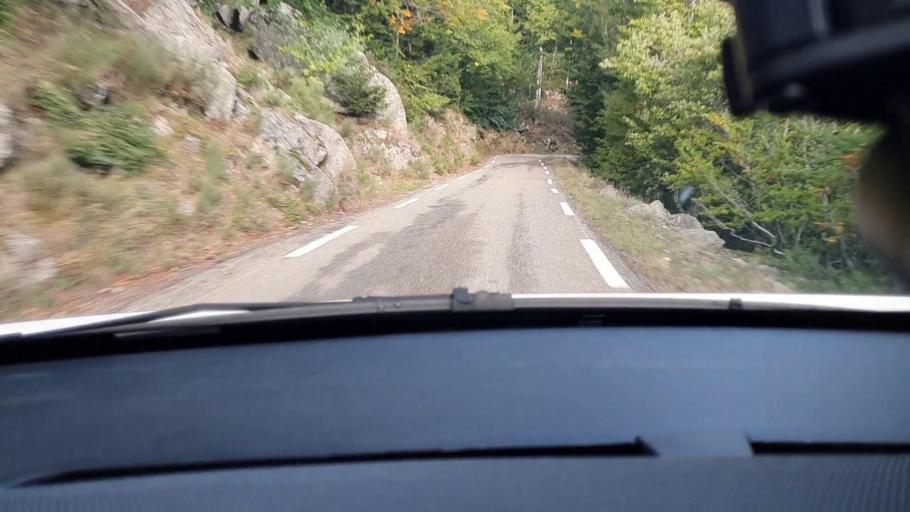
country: FR
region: Languedoc-Roussillon
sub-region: Departement du Gard
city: Branoux-les-Taillades
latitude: 44.3650
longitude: 3.9181
